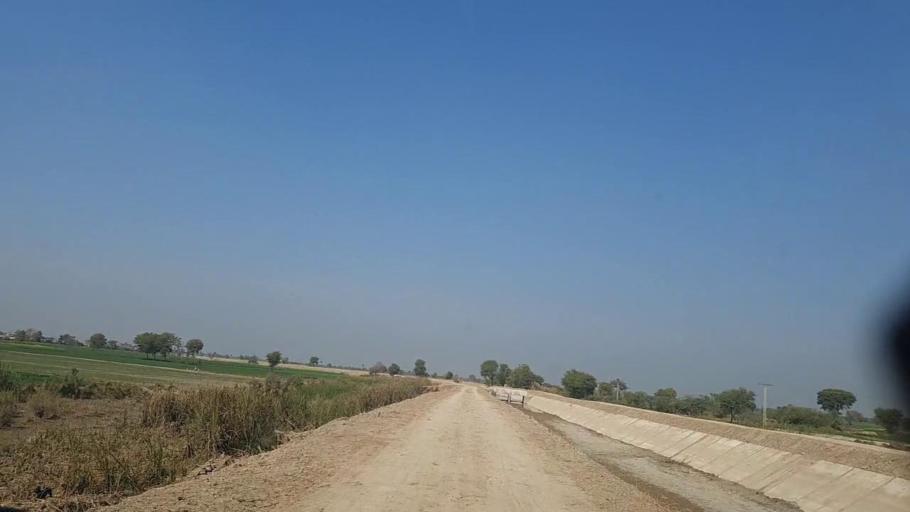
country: PK
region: Sindh
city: Sakrand
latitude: 26.1613
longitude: 68.3262
